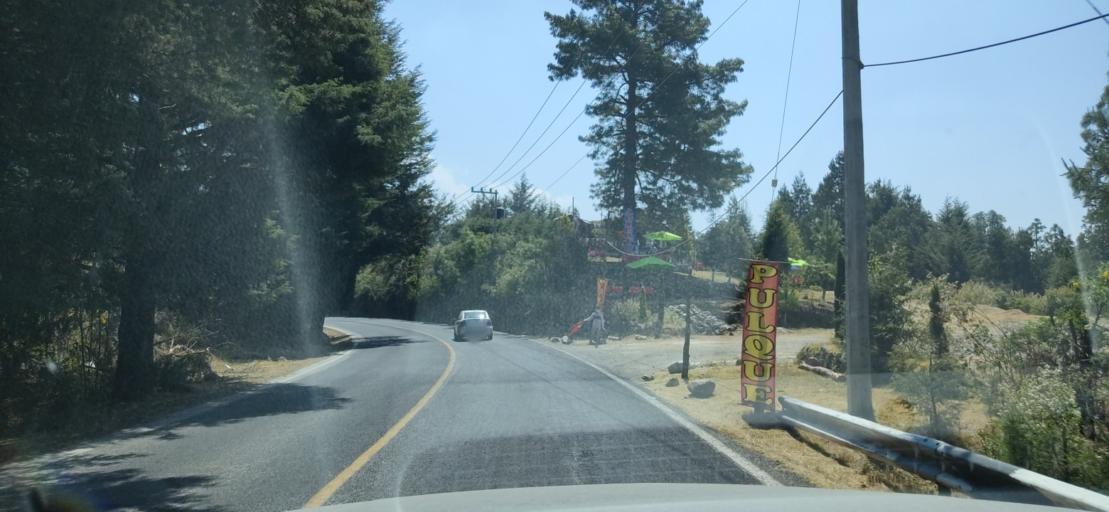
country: MX
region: Mexico
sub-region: Ocoyoacac
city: San Jeronimo Acazulco
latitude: 19.2539
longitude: -99.3778
